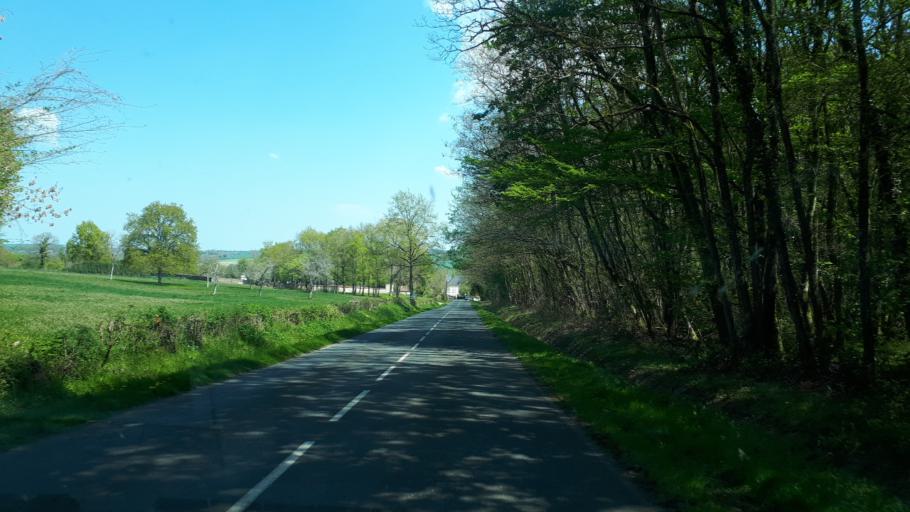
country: FR
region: Centre
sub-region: Departement du Cher
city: Rians
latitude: 47.3003
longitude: 2.6812
